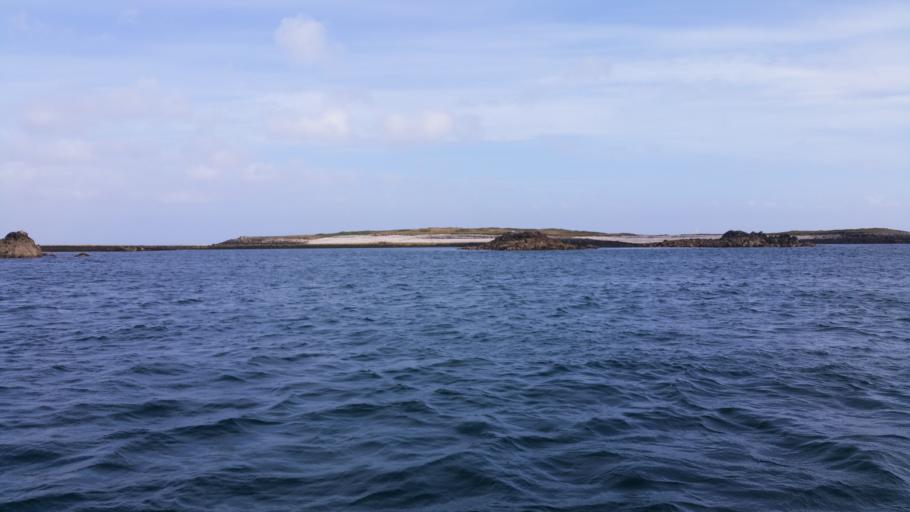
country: FR
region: Brittany
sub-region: Departement du Finistere
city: Le Conquet
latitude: 48.4058
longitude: -4.9532
